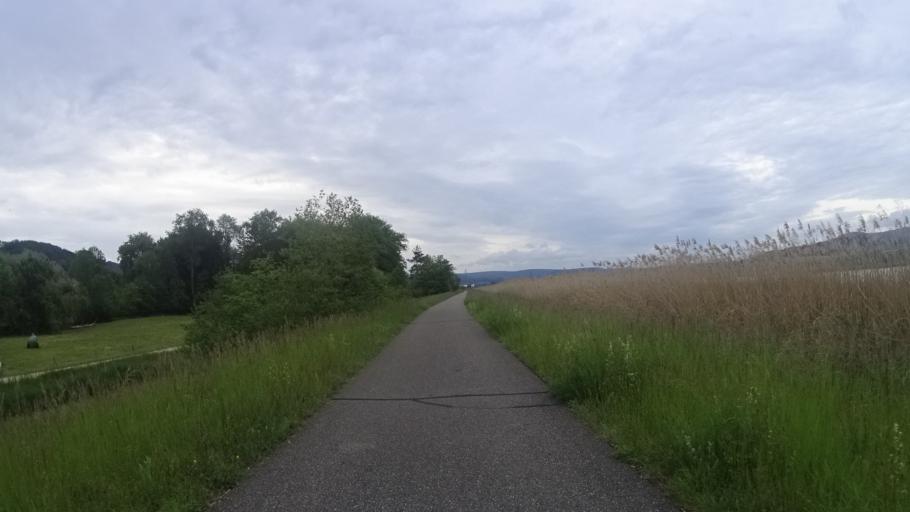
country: CH
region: Aargau
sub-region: Bezirk Zurzach
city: Koblenz
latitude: 47.5919
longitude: 8.2305
